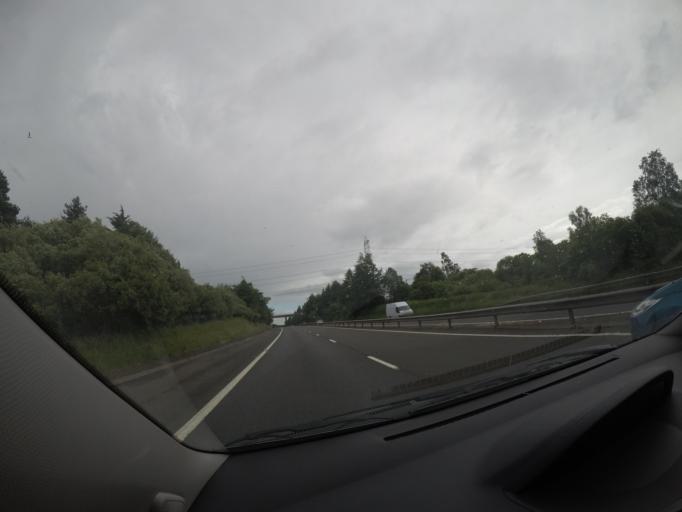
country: GB
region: Scotland
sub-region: Falkirk
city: Dunipace
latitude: 56.0107
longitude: -3.9198
